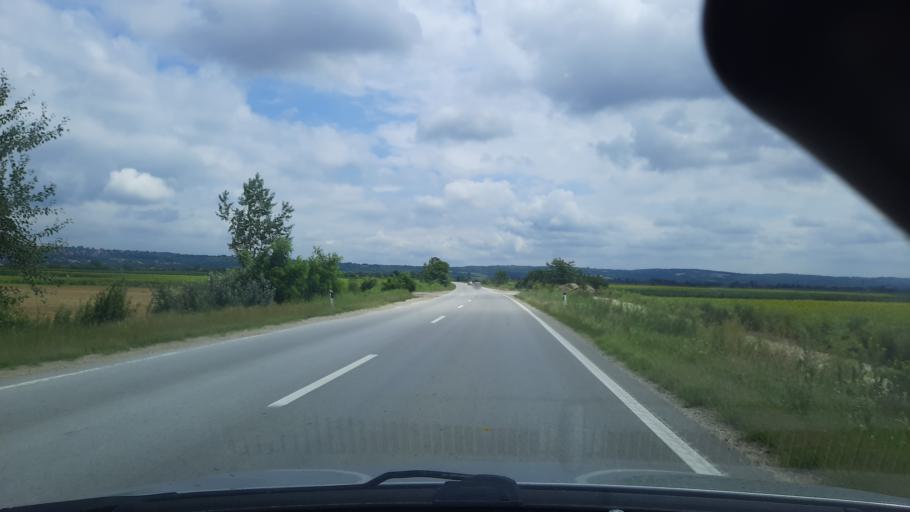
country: RS
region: Central Serbia
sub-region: Branicevski Okrug
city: Pozarevac
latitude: 44.5958
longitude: 21.1592
